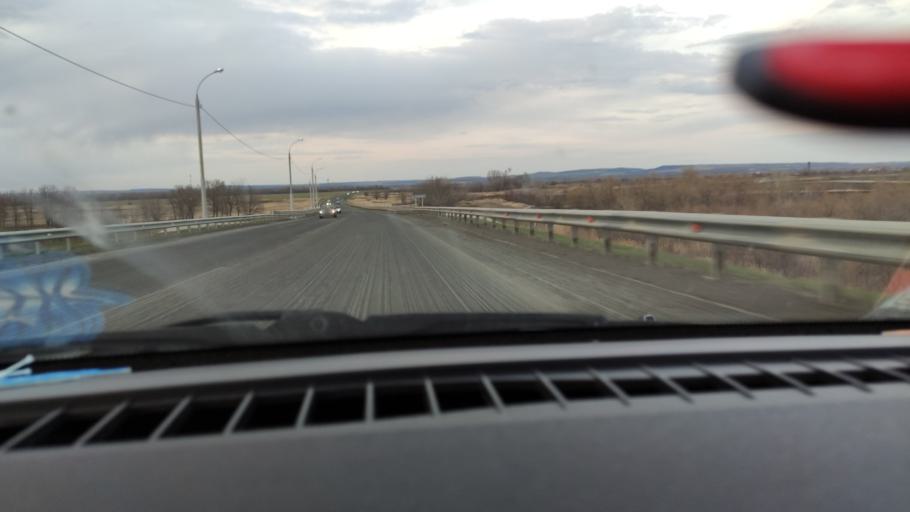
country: RU
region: Saratov
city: Yelshanka
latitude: 51.8078
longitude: 46.1965
